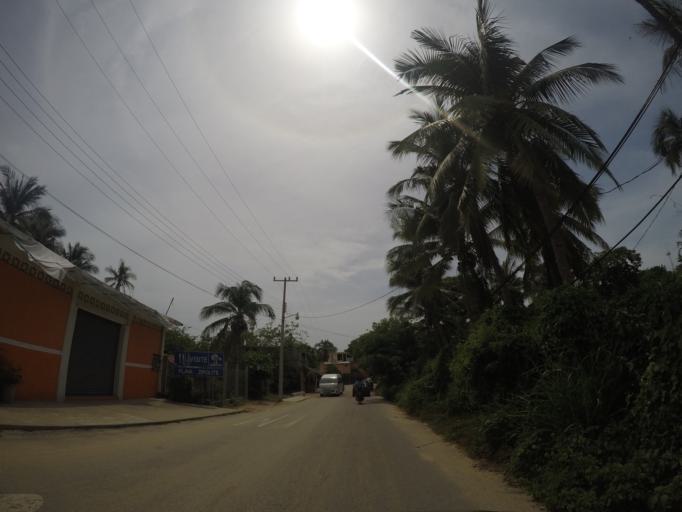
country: MX
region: Oaxaca
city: San Pedro Pochutla
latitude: 15.6617
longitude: -96.5082
